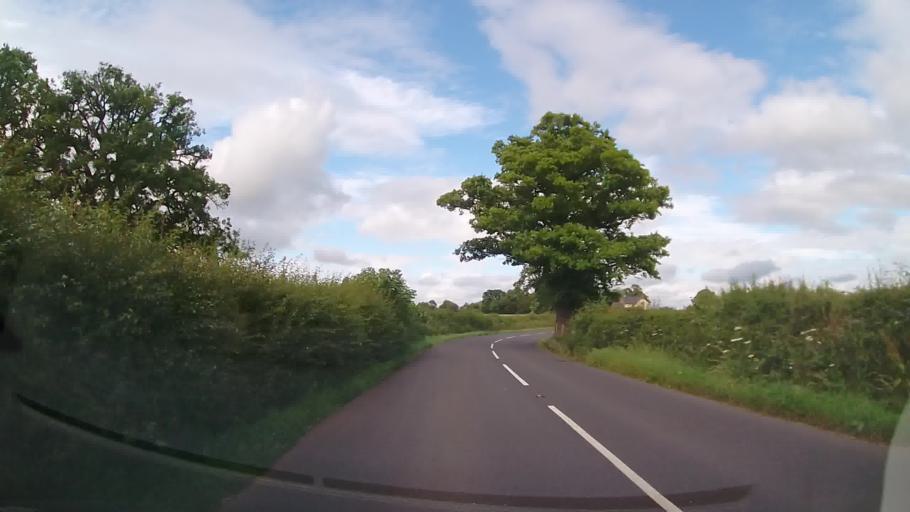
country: GB
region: England
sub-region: Shropshire
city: Wem
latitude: 52.8653
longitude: -2.7729
